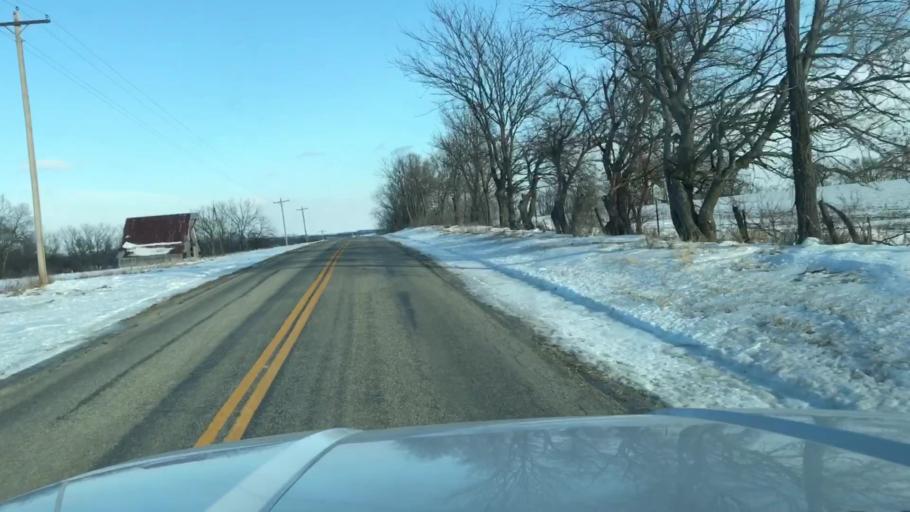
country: US
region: Missouri
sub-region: Holt County
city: Oregon
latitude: 40.1008
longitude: -95.0156
